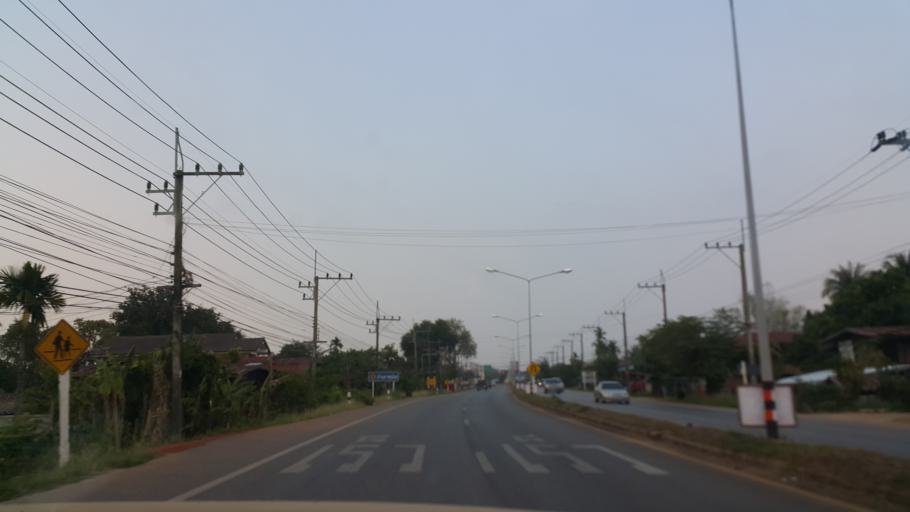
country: TH
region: Nakhon Phanom
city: Renu Nakhon
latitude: 17.0147
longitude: 104.7250
